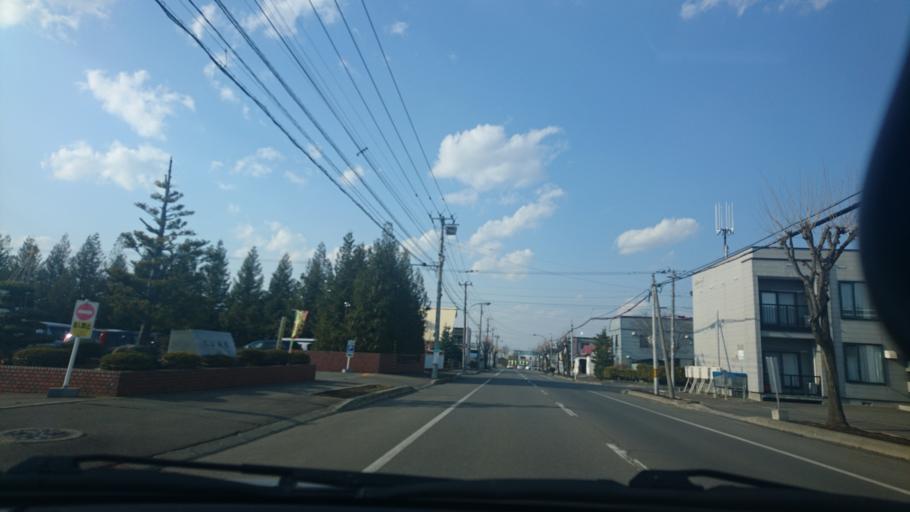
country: JP
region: Hokkaido
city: Obihiro
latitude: 42.9203
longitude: 143.1509
